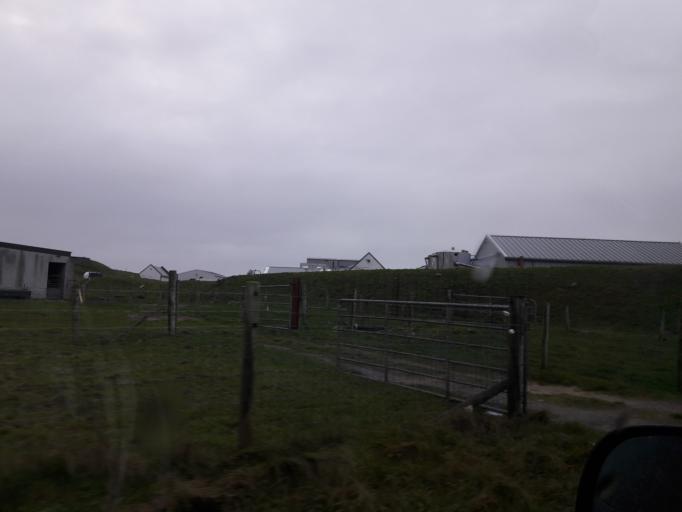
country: IE
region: Ulster
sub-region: County Donegal
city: Ramelton
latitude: 55.2622
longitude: -7.6885
